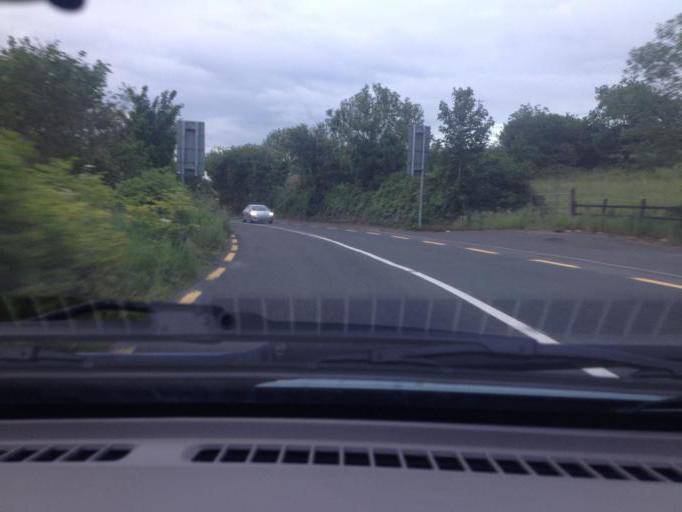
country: IE
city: Ballisodare
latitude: 54.2167
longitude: -8.5082
